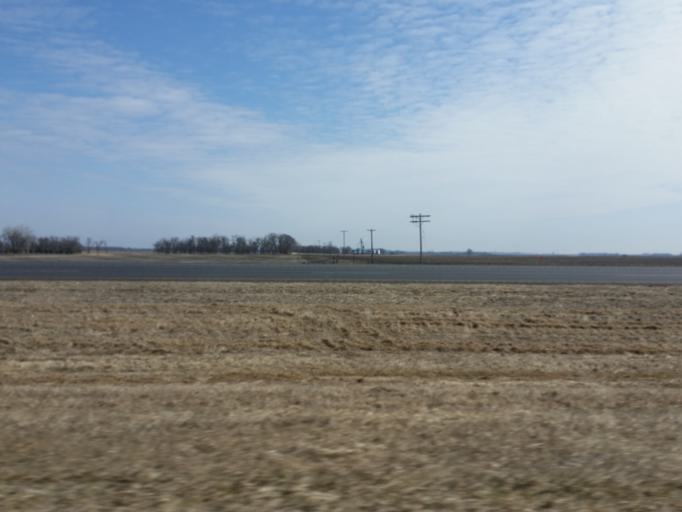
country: US
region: South Dakota
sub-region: Roberts County
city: Sisseton
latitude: 45.9505
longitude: -96.8363
